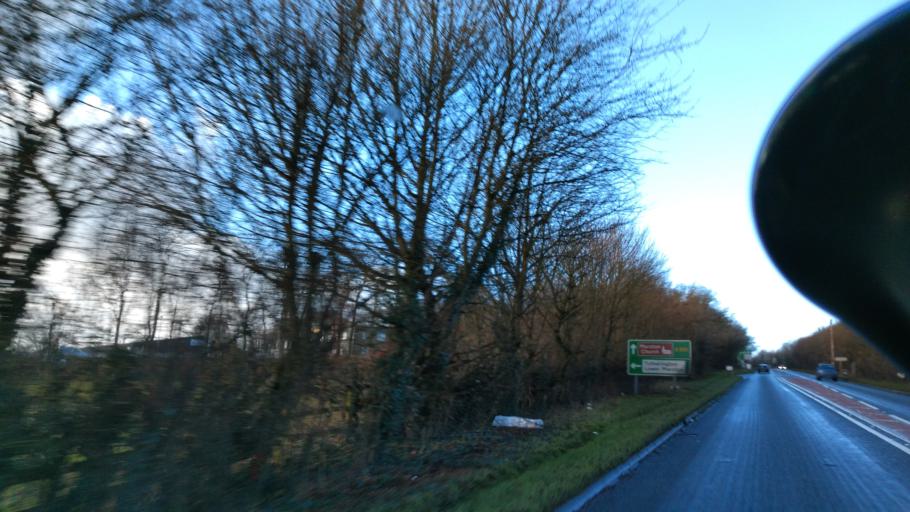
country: GB
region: England
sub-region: Somerset
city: Frome
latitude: 51.2101
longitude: -2.3354
